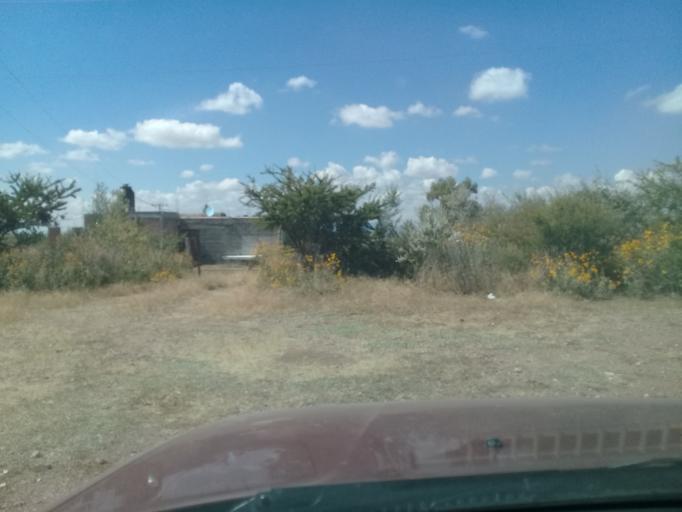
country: MX
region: Aguascalientes
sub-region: Aguascalientes
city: San Sebastian [Fraccionamiento]
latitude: 21.7814
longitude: -102.2505
